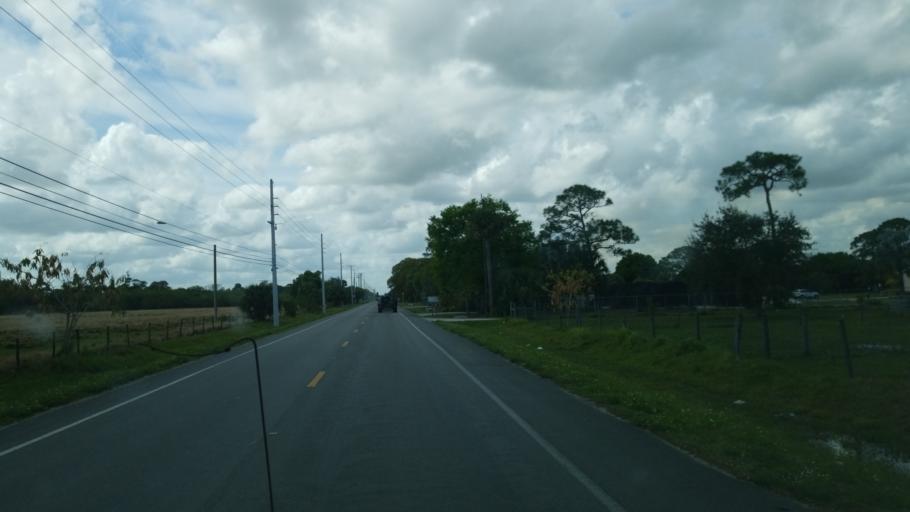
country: US
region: Florida
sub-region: Saint Lucie County
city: Lakewood Park
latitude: 27.4476
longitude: -80.4687
